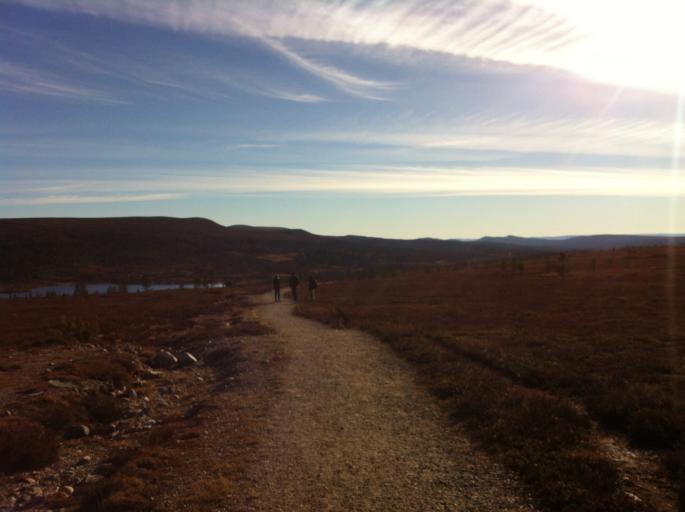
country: NO
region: Hedmark
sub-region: Engerdal
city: Engerdal
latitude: 62.1141
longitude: 12.2691
